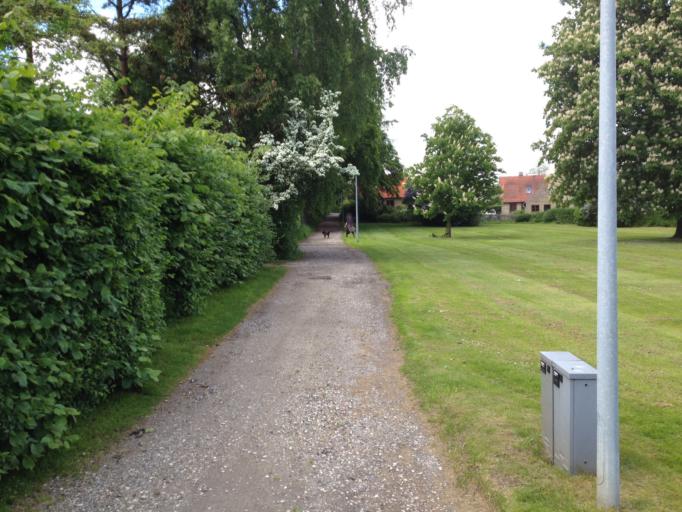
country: DK
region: Capital Region
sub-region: Fredensborg Kommune
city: Niva
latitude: 55.9296
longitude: 12.5088
